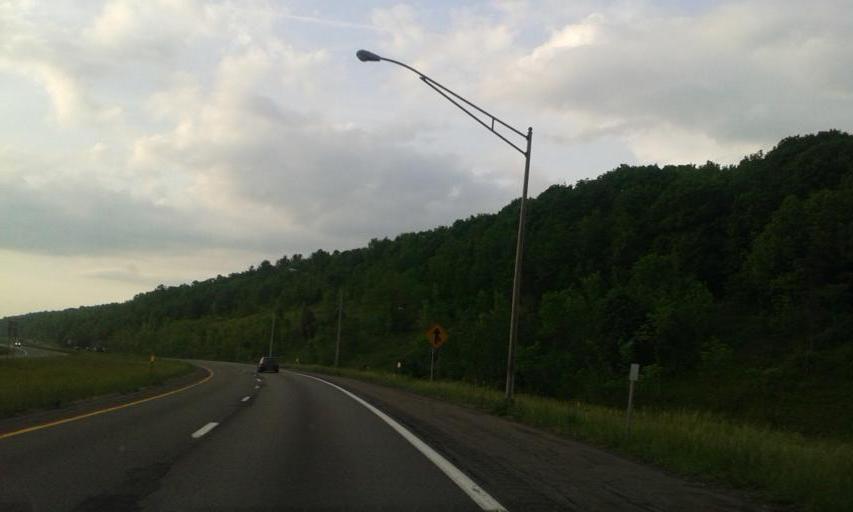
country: US
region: New York
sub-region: Broome County
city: Port Dickinson
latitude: 42.1658
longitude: -75.8957
